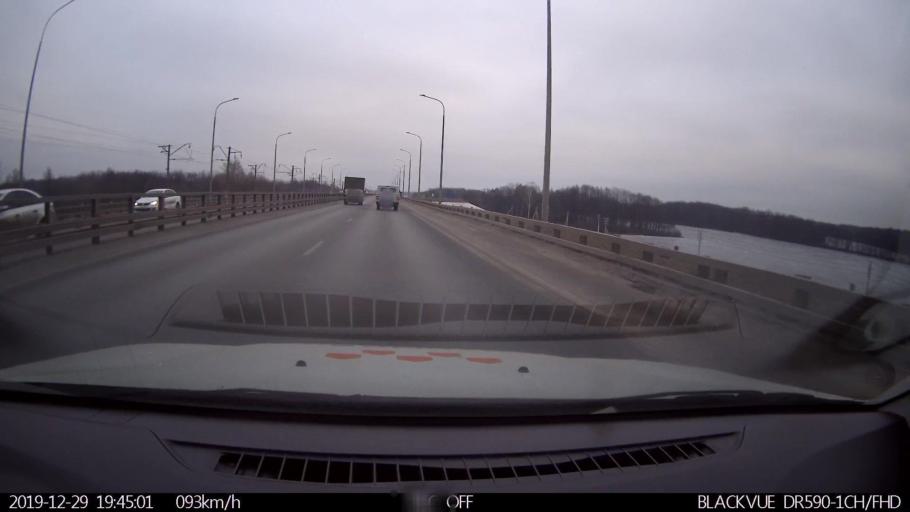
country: RU
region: Nizjnij Novgorod
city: Neklyudovo
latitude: 56.3839
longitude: 43.9637
